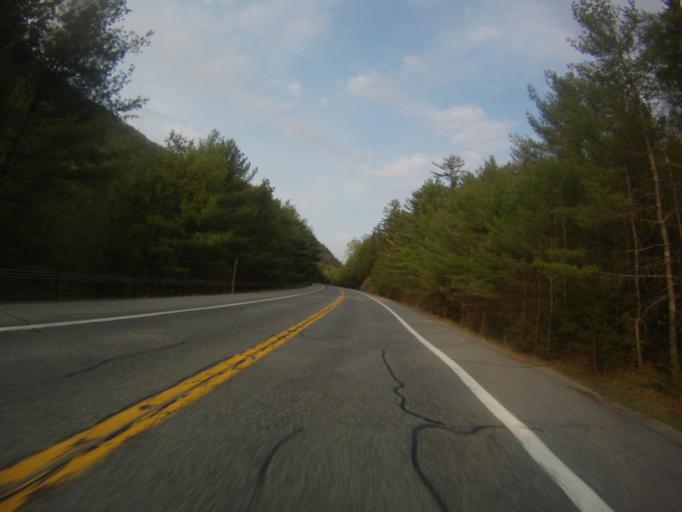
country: US
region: New York
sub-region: Essex County
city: Ticonderoga
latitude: 43.7406
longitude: -73.6559
